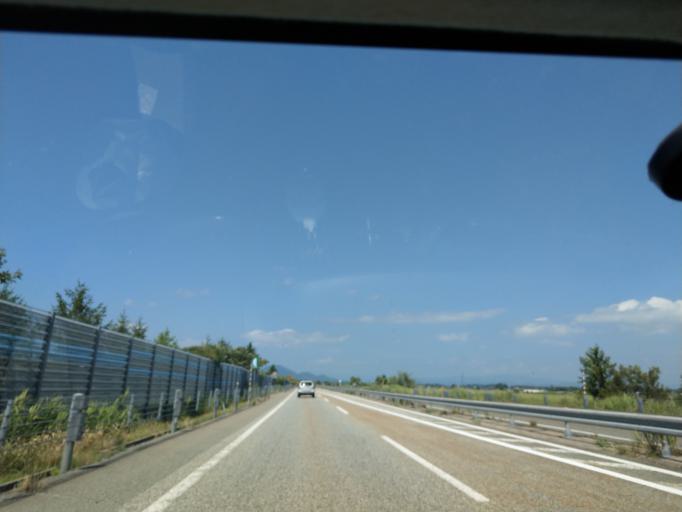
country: JP
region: Akita
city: Omagari
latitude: 39.3704
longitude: 140.4851
